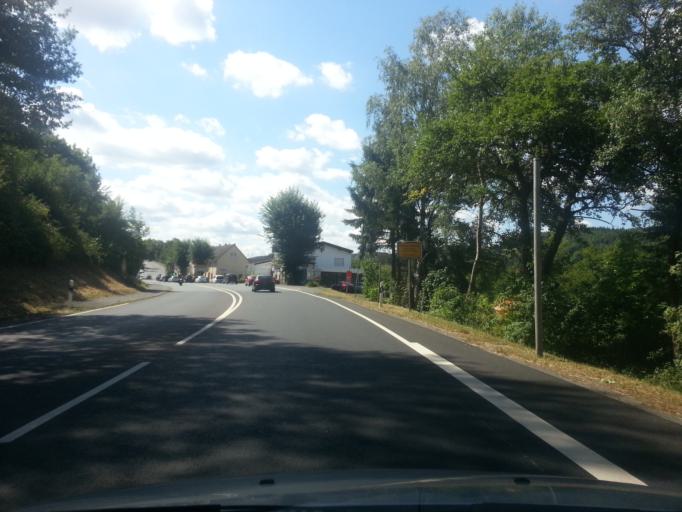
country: DE
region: Hesse
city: Hochst im Odenwald
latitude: 49.7733
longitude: 8.9916
